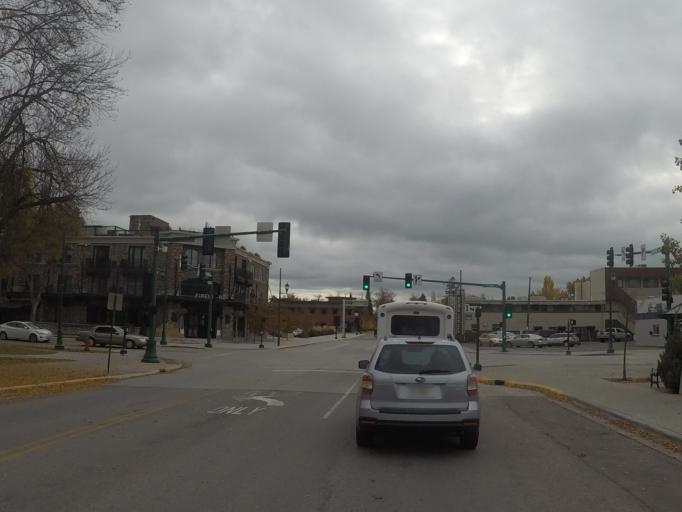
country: US
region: Montana
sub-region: Flathead County
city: Whitefish
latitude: 48.4110
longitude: -114.3353
